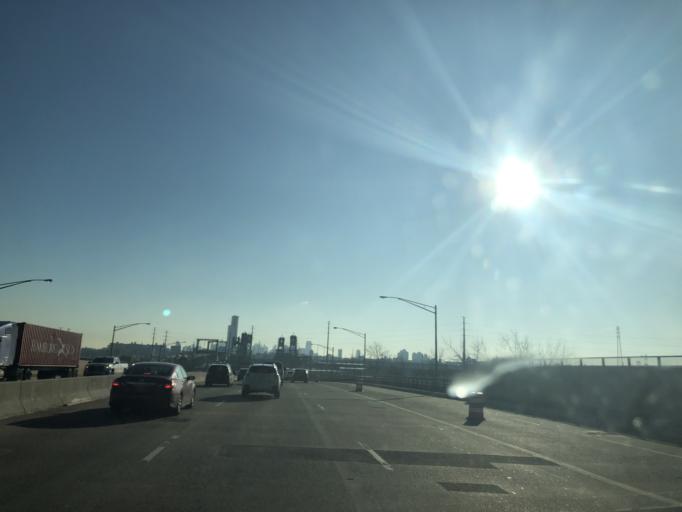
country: US
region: New Jersey
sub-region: Hudson County
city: Jersey City
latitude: 40.7457
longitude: -74.0942
